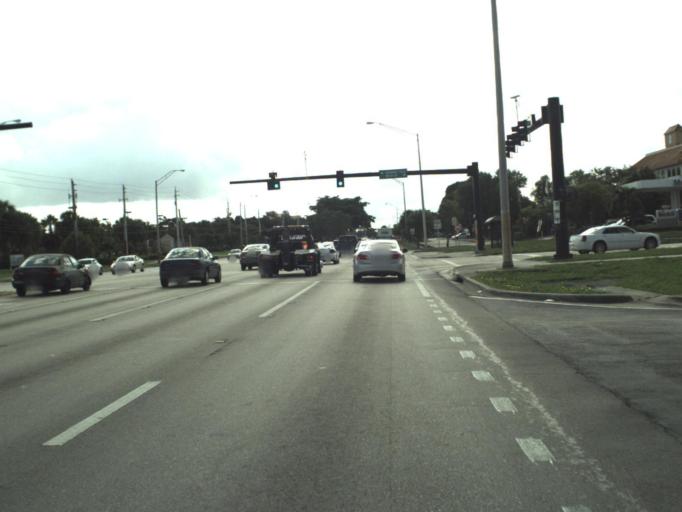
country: US
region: Florida
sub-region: Broward County
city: Lauderdale Lakes
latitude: 26.1646
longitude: -80.2326
